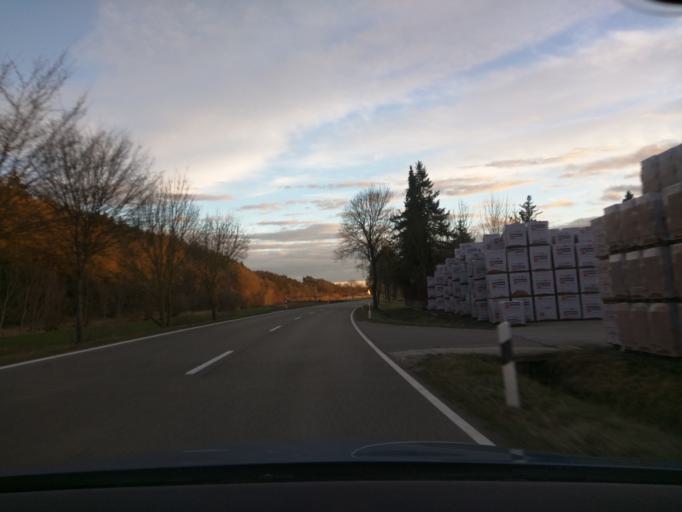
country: DE
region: Bavaria
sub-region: Upper Bavaria
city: Attenkirchen
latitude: 48.4765
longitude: 11.7595
